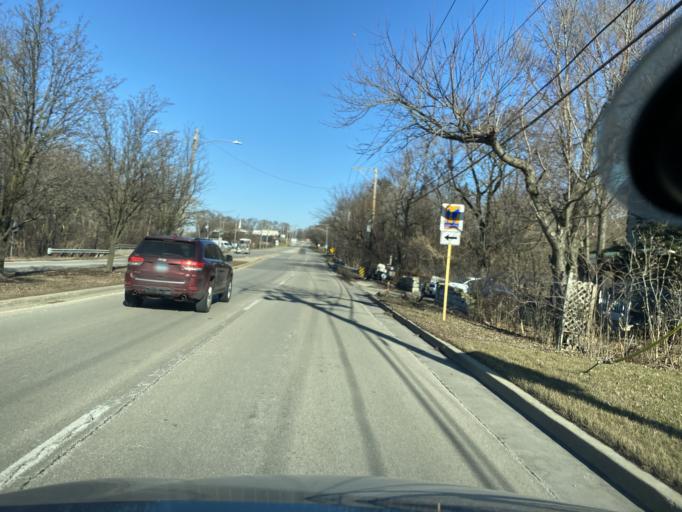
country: US
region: Illinois
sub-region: Will County
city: Lockport
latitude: 41.6001
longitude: -88.0522
